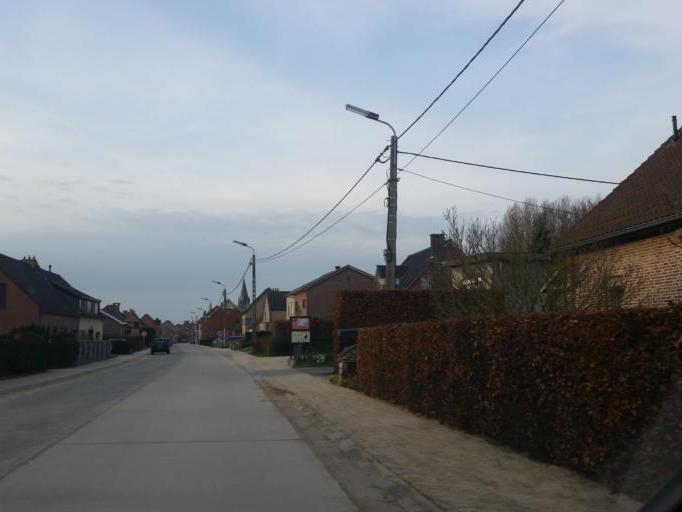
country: BE
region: Flanders
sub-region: Provincie Antwerpen
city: Mechelen
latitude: 51.0571
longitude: 4.4912
